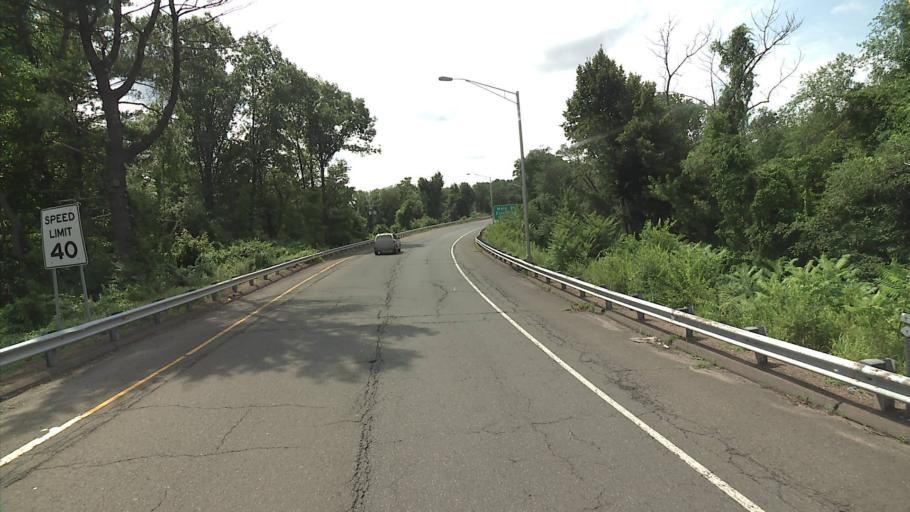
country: US
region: Connecticut
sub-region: Middlesex County
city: Middletown
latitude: 41.5565
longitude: -72.6431
